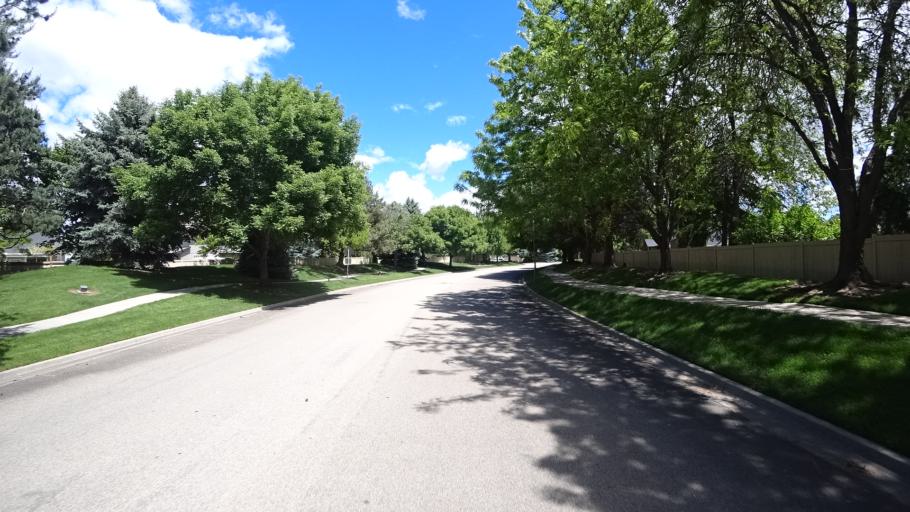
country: US
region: Idaho
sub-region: Ada County
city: Eagle
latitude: 43.6583
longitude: -116.3570
